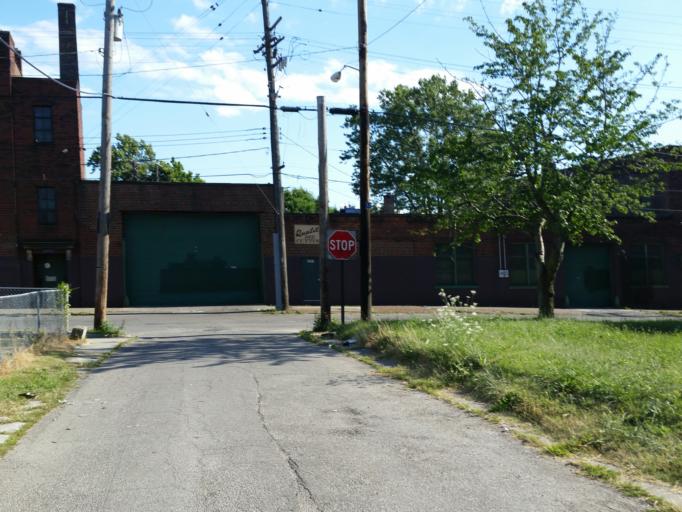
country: US
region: Ohio
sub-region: Cuyahoga County
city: Cleveland
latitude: 41.4756
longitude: -81.7010
